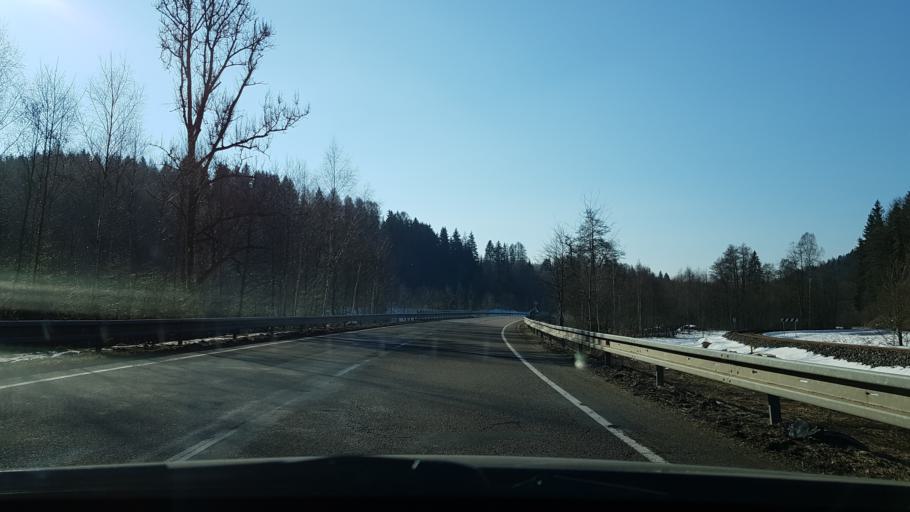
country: CZ
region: Olomoucky
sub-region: Okres Sumperk
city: Stare Mesto
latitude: 50.1208
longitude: 17.0085
